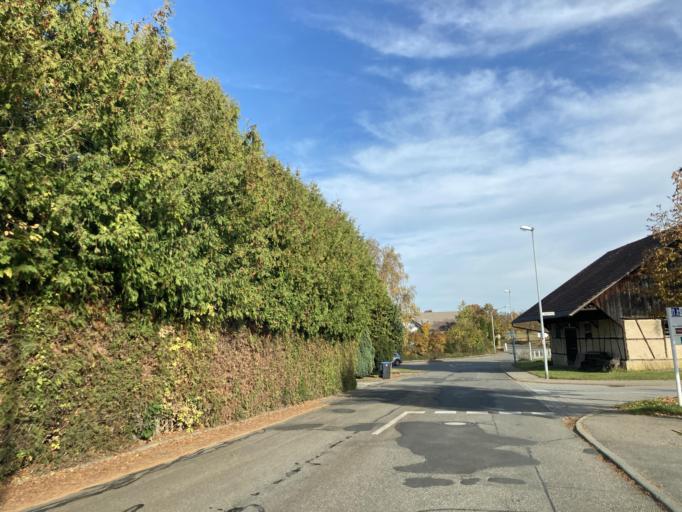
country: DE
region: Baden-Wuerttemberg
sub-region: Tuebingen Region
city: Bodelshausen
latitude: 48.3974
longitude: 8.9766
